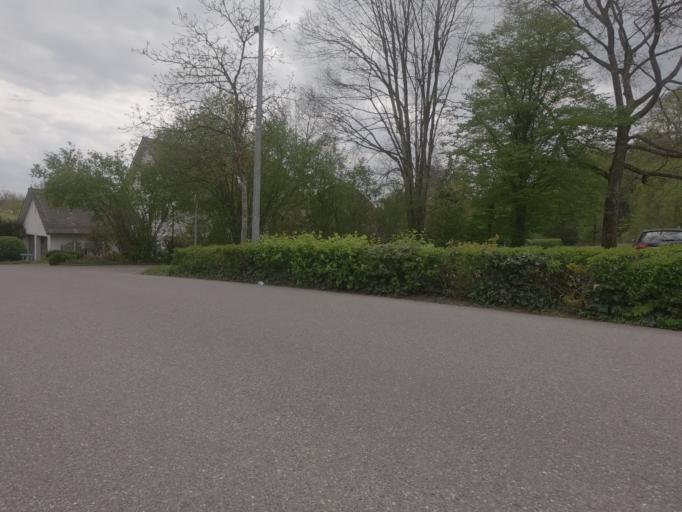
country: CH
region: Solothurn
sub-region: Bezirk Solothurn
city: Solothurn
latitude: 47.2206
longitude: 7.5431
